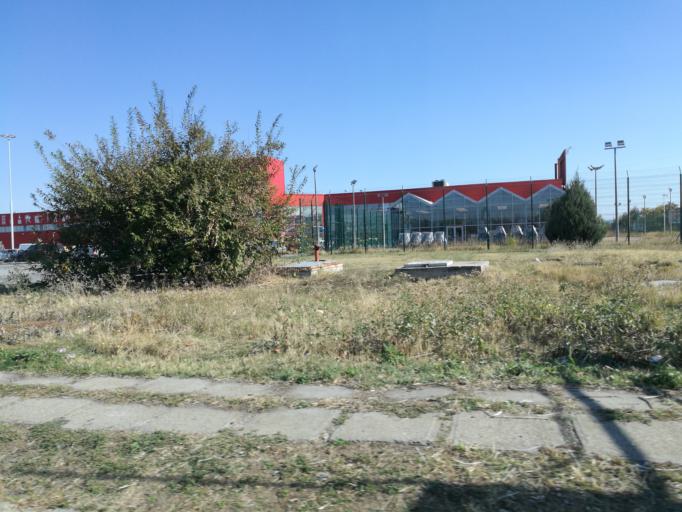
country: RO
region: Ilfov
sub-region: Comuna Chiajna
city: Chiajna
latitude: 44.4383
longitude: 25.9590
